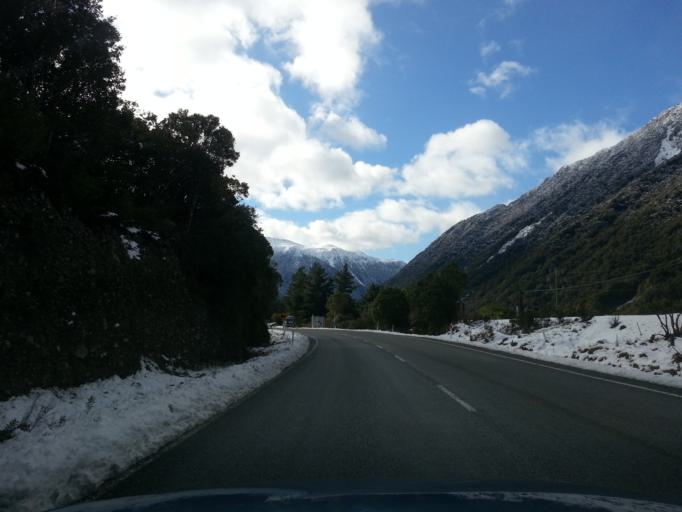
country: NZ
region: West Coast
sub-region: Grey District
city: Greymouth
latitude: -42.8458
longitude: 171.5598
